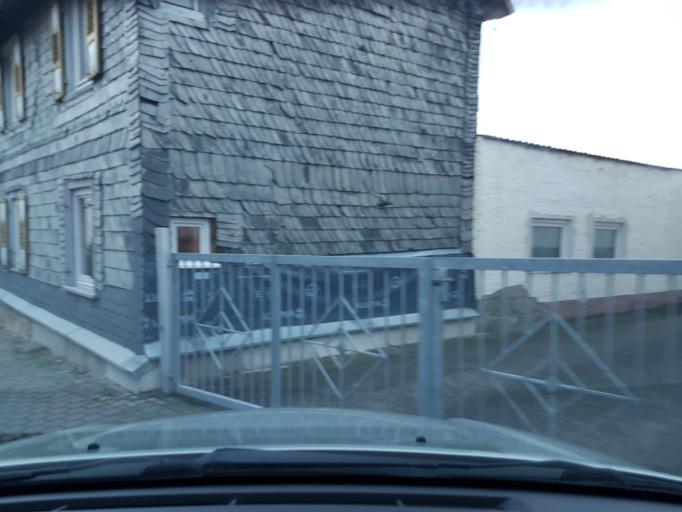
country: DE
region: Hesse
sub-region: Regierungsbezirk Darmstadt
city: Eltville
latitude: 50.0599
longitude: 8.1125
